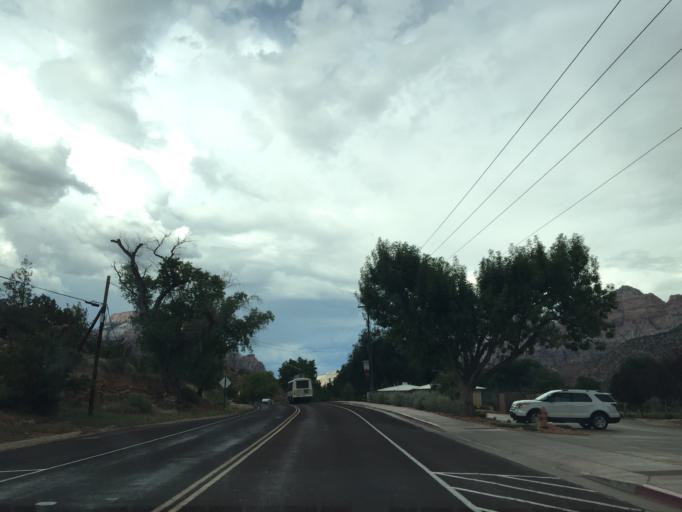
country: US
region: Utah
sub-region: Washington County
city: Hildale
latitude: 37.1800
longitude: -113.0067
